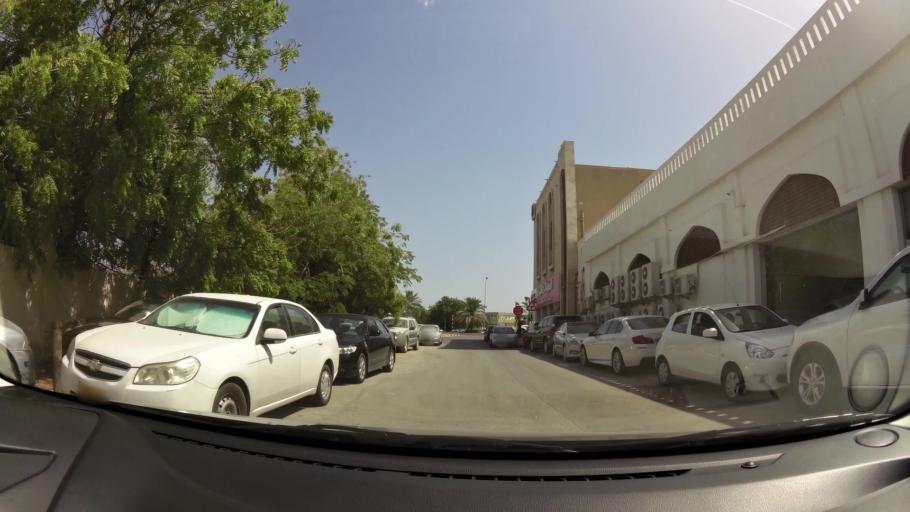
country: OM
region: Muhafazat Masqat
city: Bawshar
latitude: 23.5965
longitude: 58.4456
